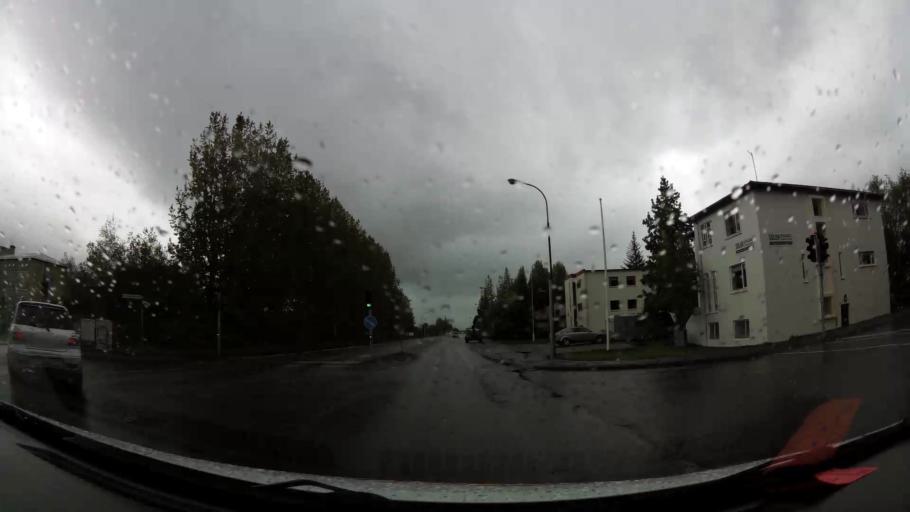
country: IS
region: Northeast
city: Akureyri
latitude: 65.6769
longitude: -18.0985
